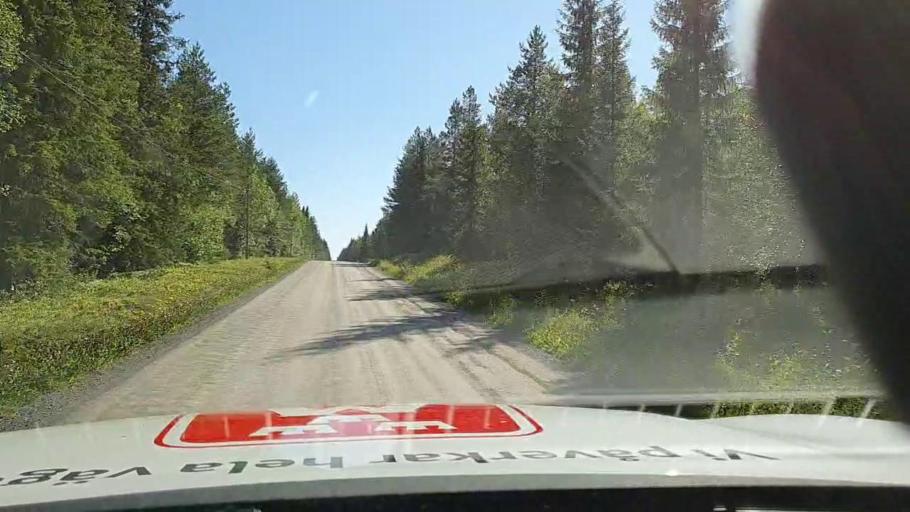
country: SE
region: Jaemtland
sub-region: Krokoms Kommun
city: Krokom
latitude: 63.6966
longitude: 14.6088
